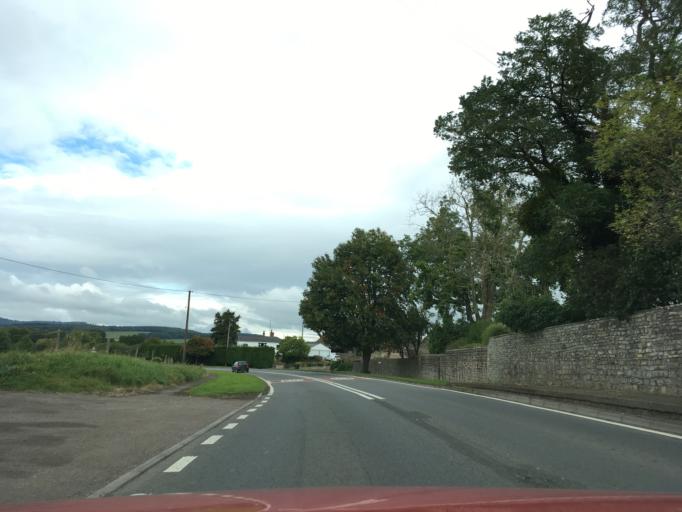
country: GB
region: England
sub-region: Gloucestershire
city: Mitcheldean
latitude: 51.8268
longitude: -2.4142
